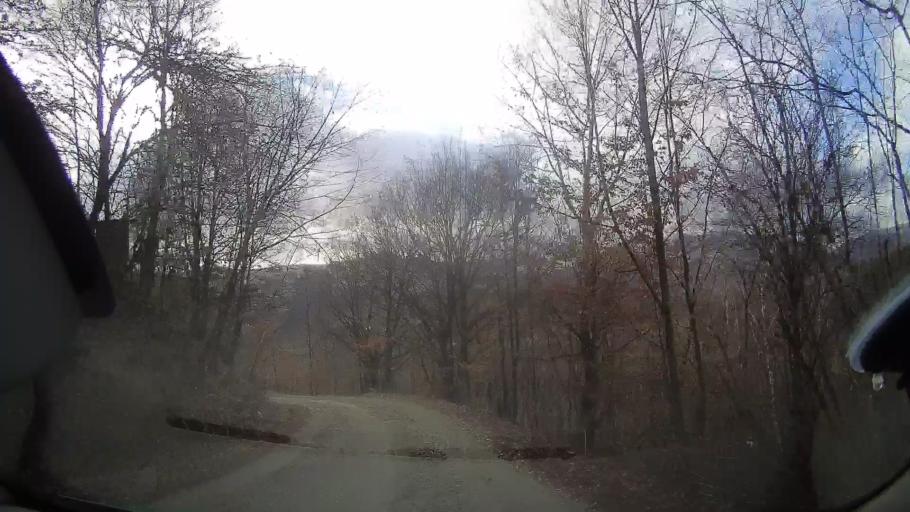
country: RO
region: Cluj
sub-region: Comuna Valea Ierii
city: Valea Ierii
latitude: 46.6816
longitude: 23.3104
